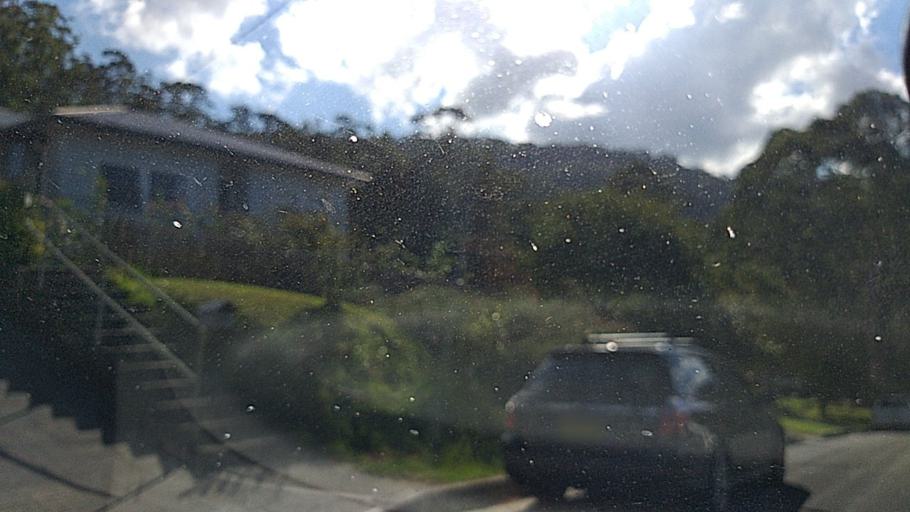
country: AU
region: New South Wales
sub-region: Wollongong
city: Cordeaux Heights
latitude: -34.4310
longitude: 150.8175
